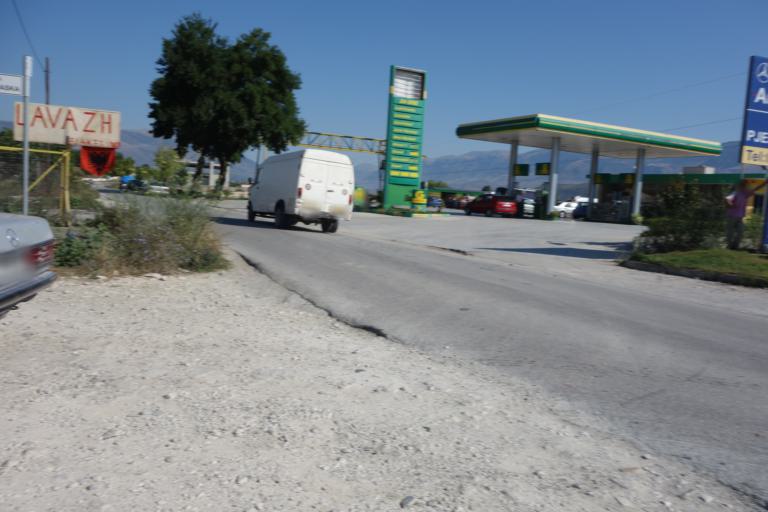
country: AL
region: Gjirokaster
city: Gjirokaster
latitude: 40.0891
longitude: 20.1392
